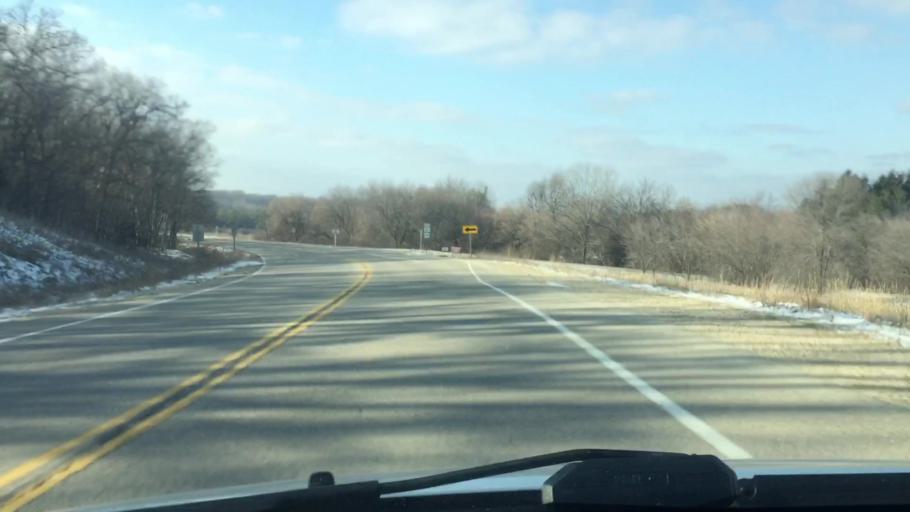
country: US
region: Wisconsin
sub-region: Waukesha County
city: Eagle
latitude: 42.8818
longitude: -88.4893
